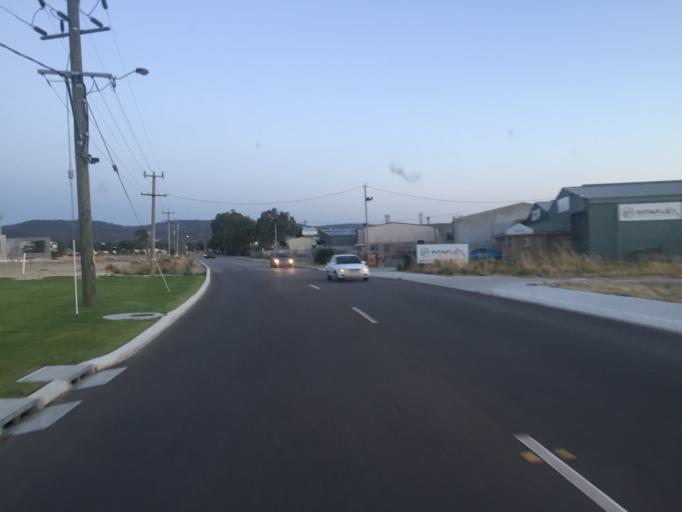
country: AU
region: Western Australia
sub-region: Gosnells
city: Maddington
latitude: -32.0325
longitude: 115.9967
